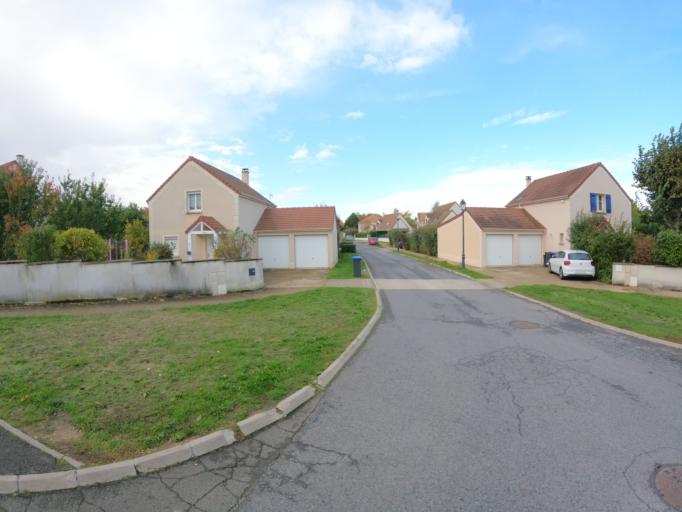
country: FR
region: Ile-de-France
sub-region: Departement de Seine-et-Marne
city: Saint-Germain-sur-Morin
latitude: 48.8781
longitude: 2.8539
